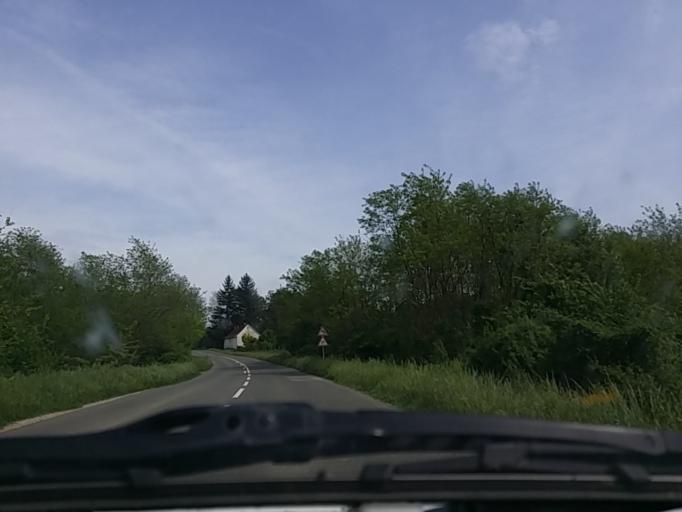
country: HU
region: Baranya
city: Vajszlo
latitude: 45.8407
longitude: 18.0519
